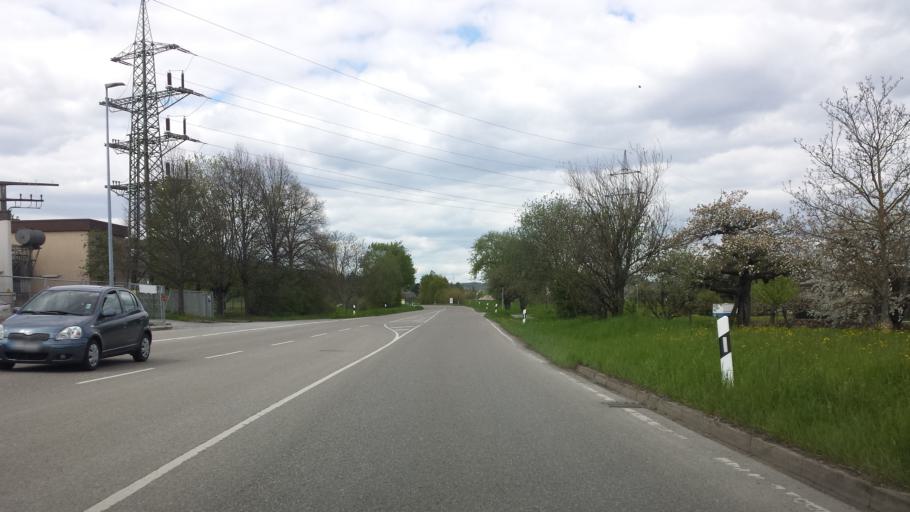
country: DE
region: Baden-Wuerttemberg
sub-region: Regierungsbezirk Stuttgart
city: Gerlingen
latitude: 48.8019
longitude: 9.0535
